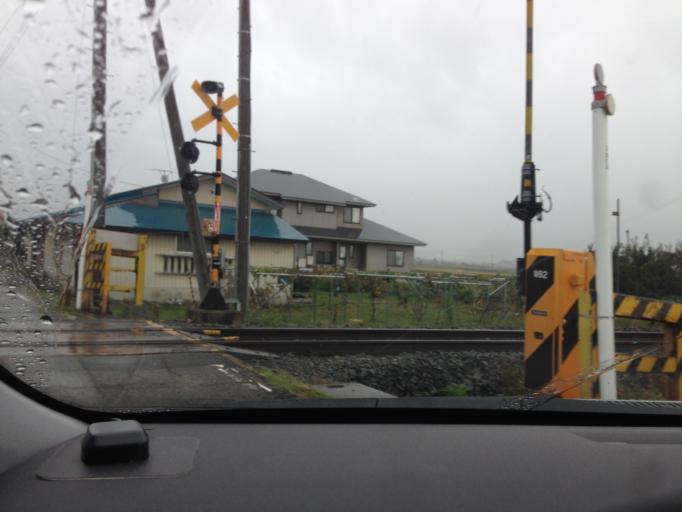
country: JP
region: Fukushima
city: Kitakata
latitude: 37.4635
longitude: 139.8724
